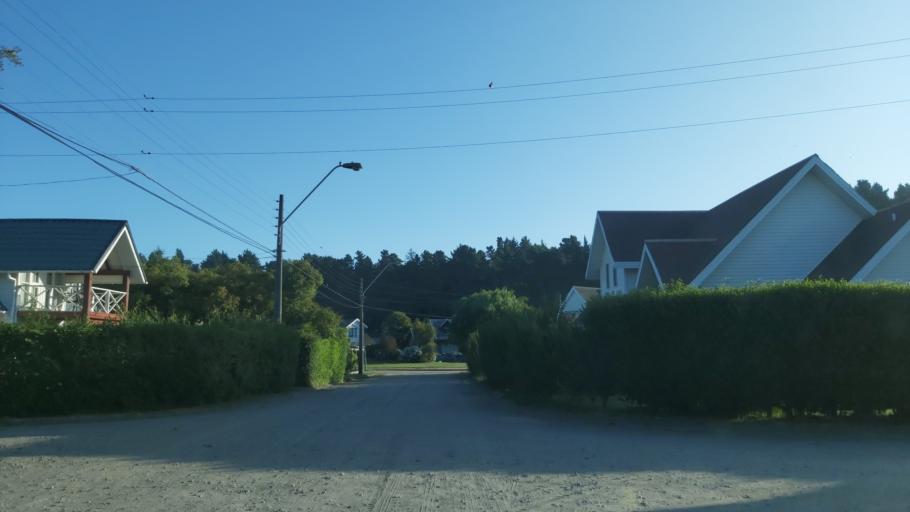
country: CL
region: Biobio
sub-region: Provincia de Concepcion
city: Tome
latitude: -36.5306
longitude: -72.9325
